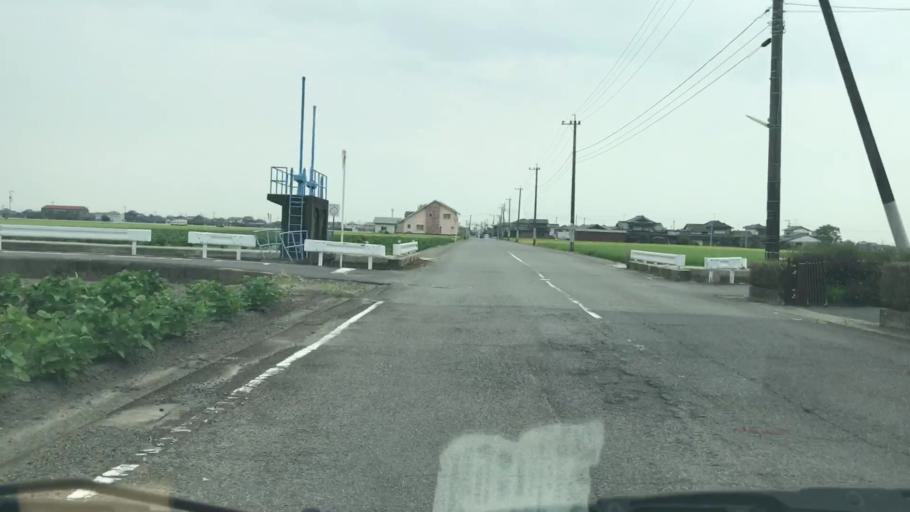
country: JP
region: Saga Prefecture
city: Saga-shi
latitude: 33.2235
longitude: 130.1766
